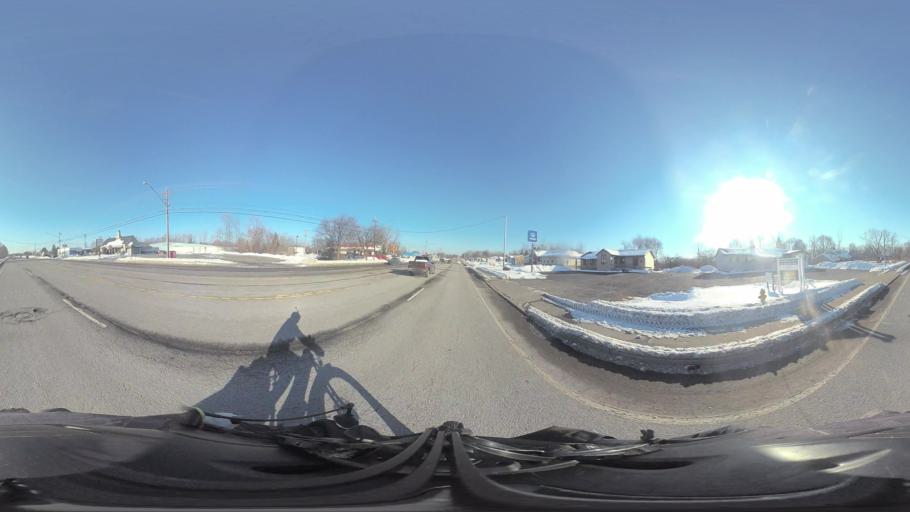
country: US
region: New York
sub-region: Monroe County
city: Rochester
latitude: 43.0759
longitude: -77.6063
